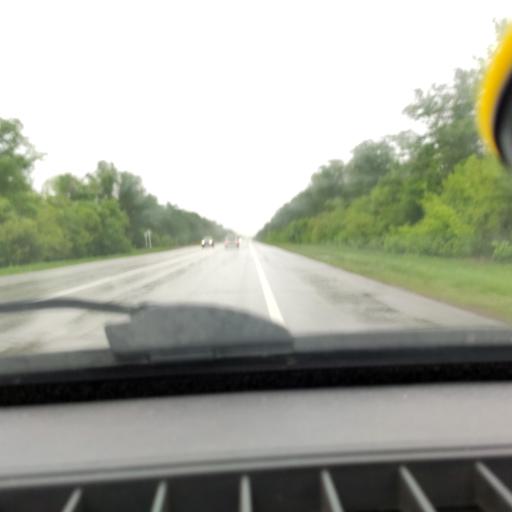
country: RU
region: Samara
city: Tol'yatti
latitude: 53.6022
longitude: 49.4094
